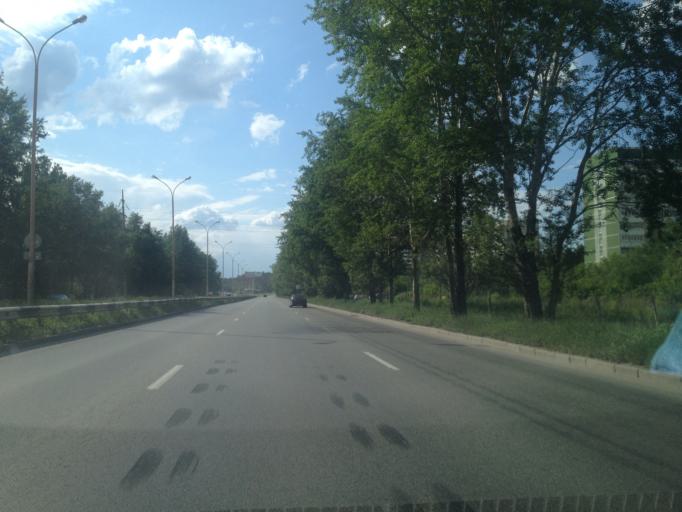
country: RU
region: Sverdlovsk
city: Sovkhoznyy
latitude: 56.7982
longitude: 60.5557
